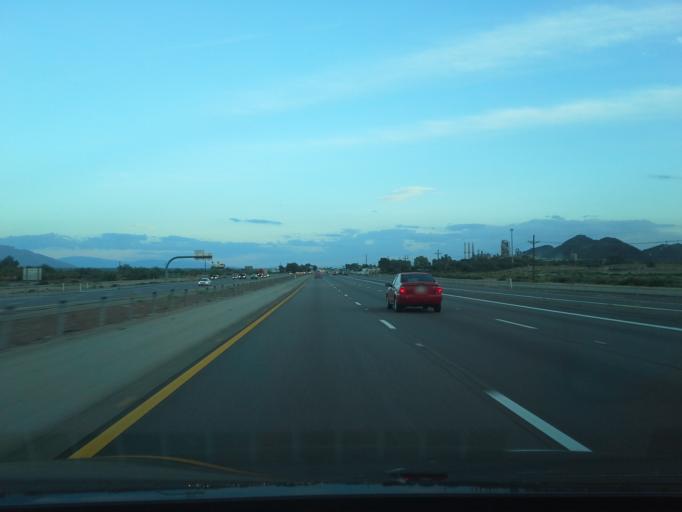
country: US
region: Arizona
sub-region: Pima County
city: Marana
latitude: 32.4224
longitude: -111.1609
